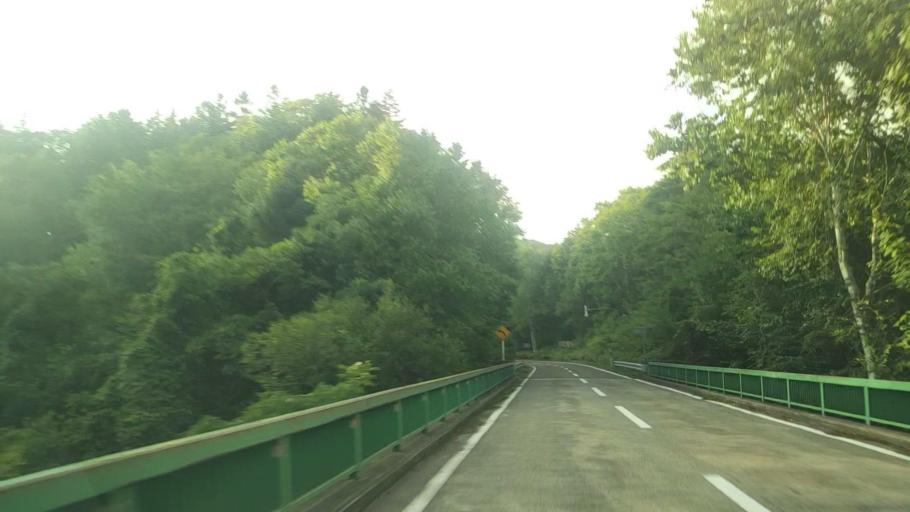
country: JP
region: Hokkaido
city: Bibai
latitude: 43.1430
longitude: 142.0911
